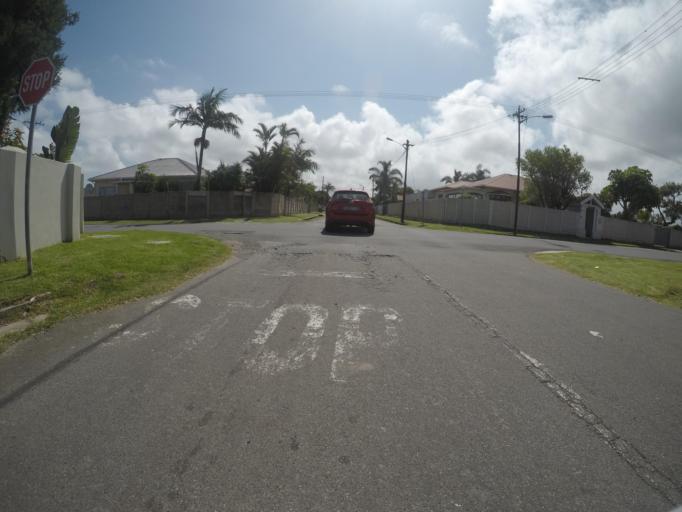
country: ZA
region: Eastern Cape
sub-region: Buffalo City Metropolitan Municipality
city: East London
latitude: -32.9828
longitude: 27.9082
